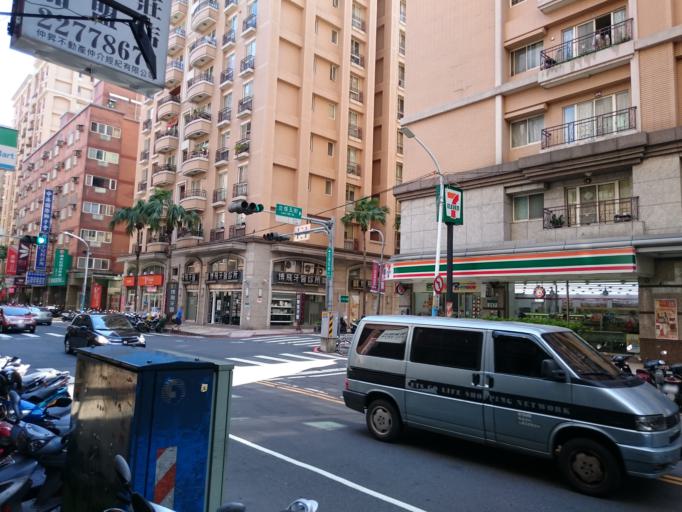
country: TW
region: Taipei
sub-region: Taipei
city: Banqiao
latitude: 25.0518
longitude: 121.4445
